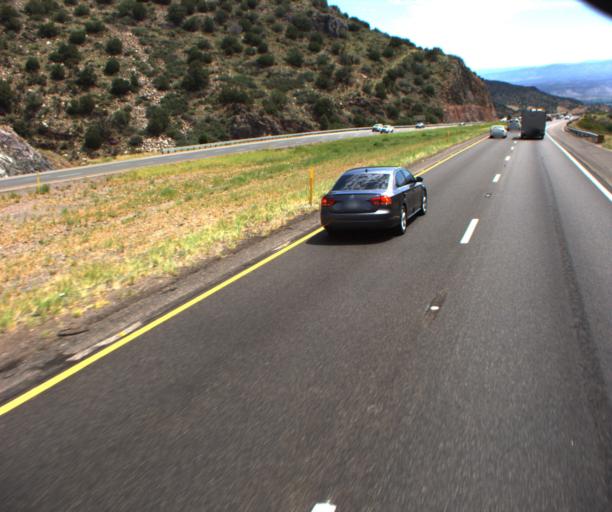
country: US
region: Arizona
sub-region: Yavapai County
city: Camp Verde
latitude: 34.5300
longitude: -111.9471
